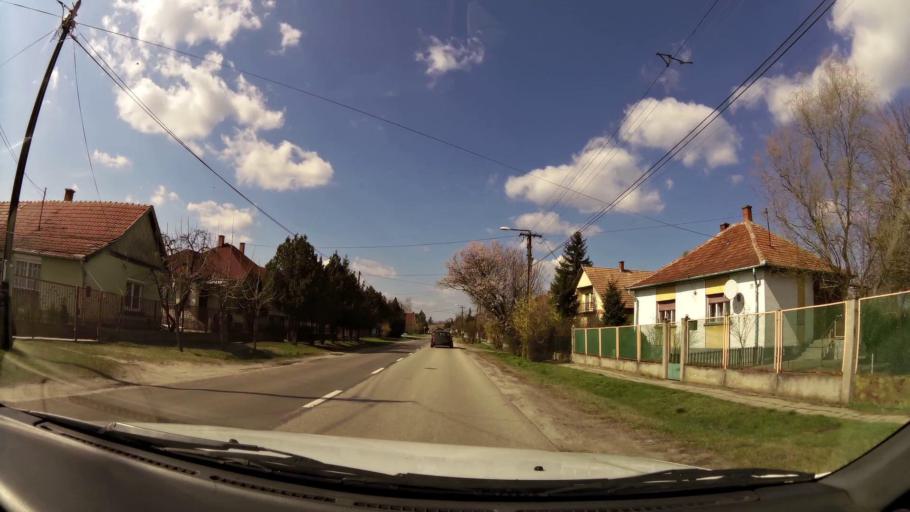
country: HU
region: Pest
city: Farmos
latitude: 47.3564
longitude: 19.8527
